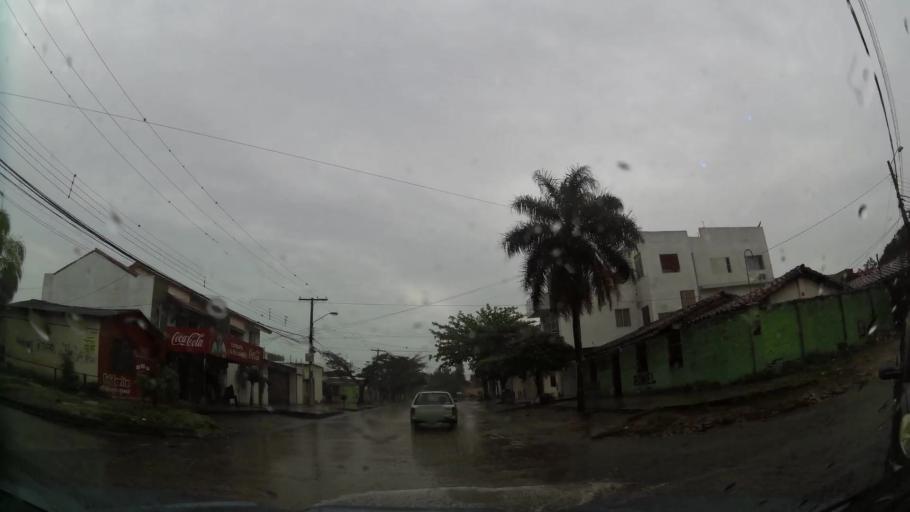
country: BO
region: Santa Cruz
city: Santa Cruz de la Sierra
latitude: -17.8008
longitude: -63.1648
